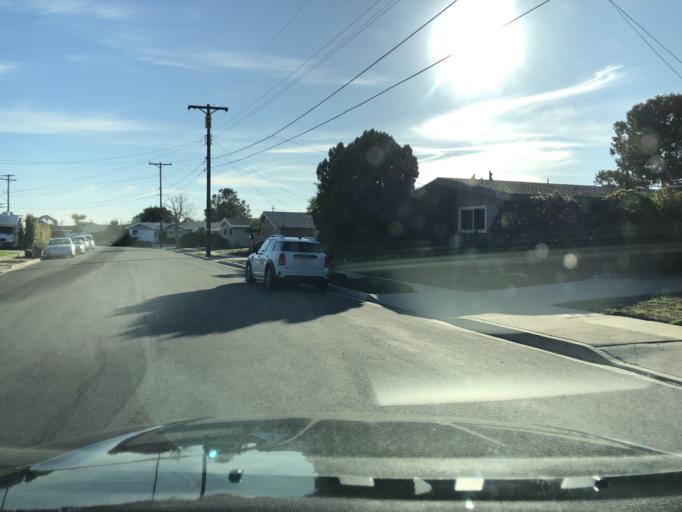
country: US
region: California
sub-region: San Diego County
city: La Jolla
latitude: 32.8193
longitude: -117.1986
